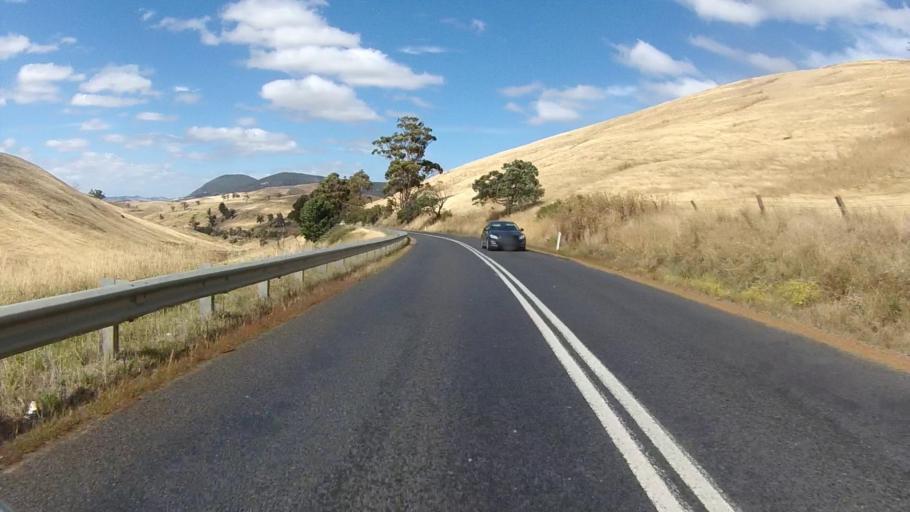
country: AU
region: Tasmania
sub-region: Brighton
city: Bridgewater
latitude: -42.5615
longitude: 147.3912
